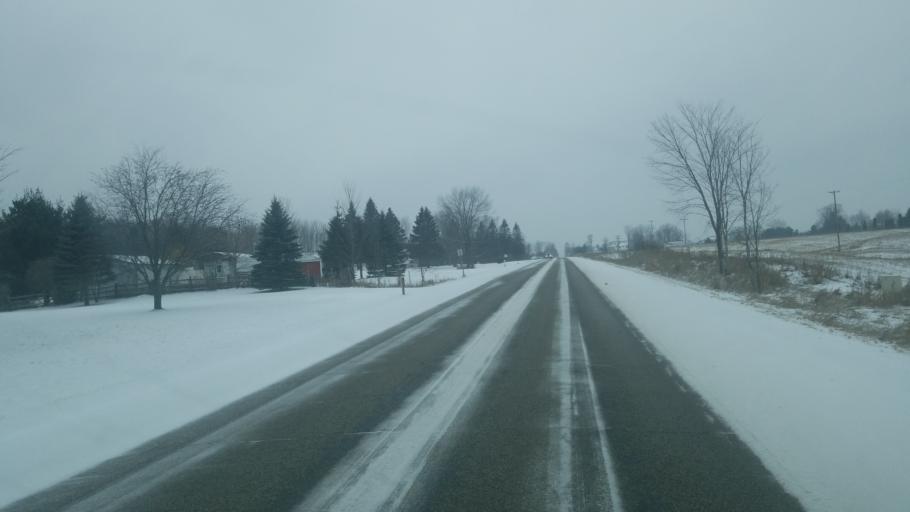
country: US
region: Michigan
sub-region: Osceola County
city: Evart
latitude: 44.1025
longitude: -85.1625
